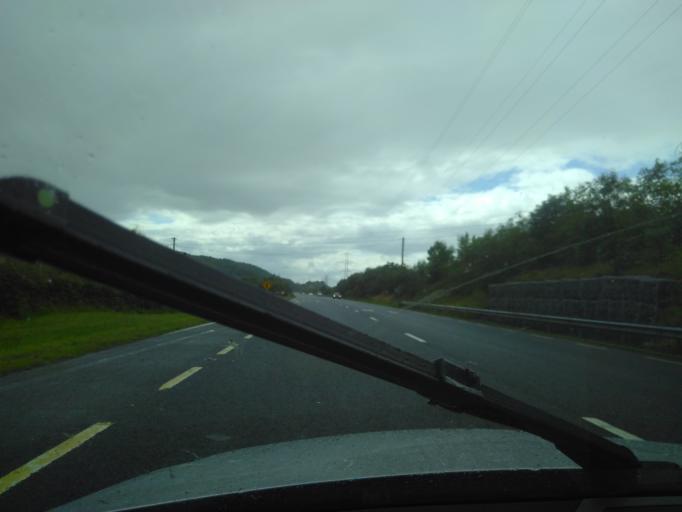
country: IE
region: Ulster
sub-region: County Donegal
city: Donegal
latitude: 54.7102
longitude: -7.9707
